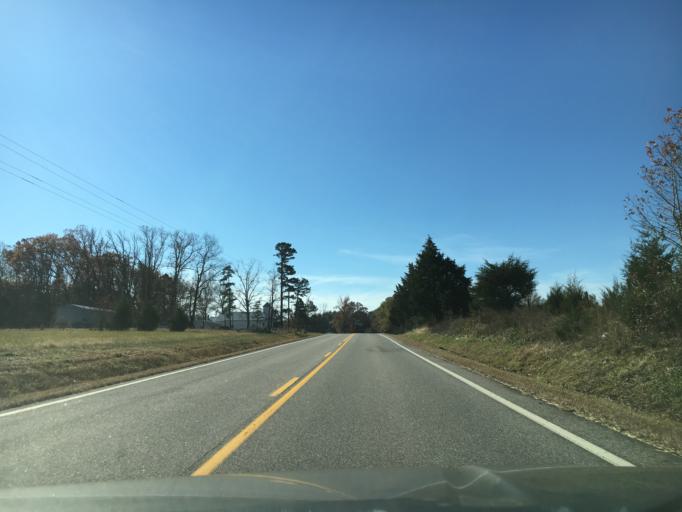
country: US
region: Virginia
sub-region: Cumberland County
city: Cumberland
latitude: 37.5321
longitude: -78.1976
